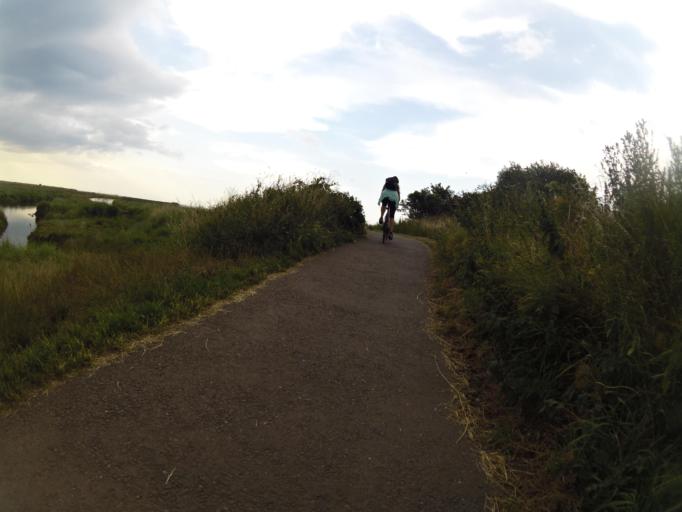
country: GB
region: Scotland
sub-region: East Lothian
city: Dunbar
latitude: 55.9979
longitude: -2.5506
